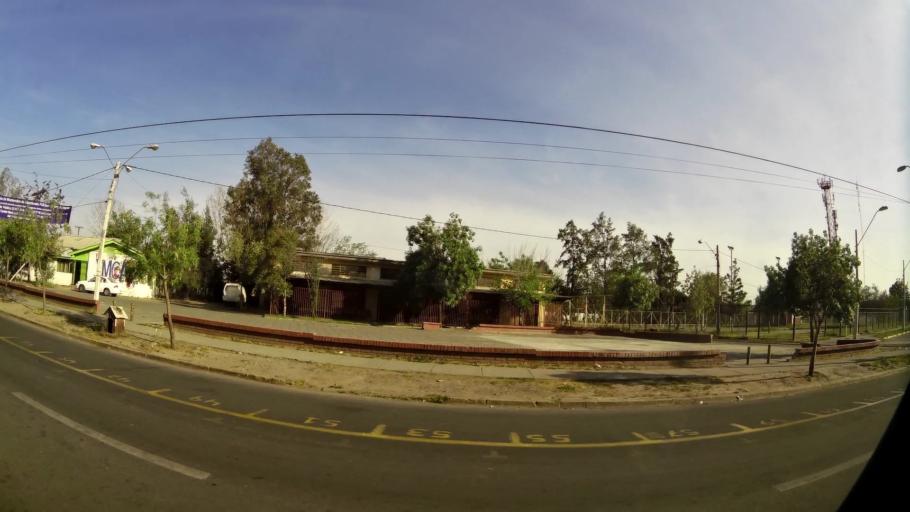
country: CL
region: Santiago Metropolitan
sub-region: Provincia de Santiago
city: Santiago
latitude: -33.5093
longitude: -70.6240
